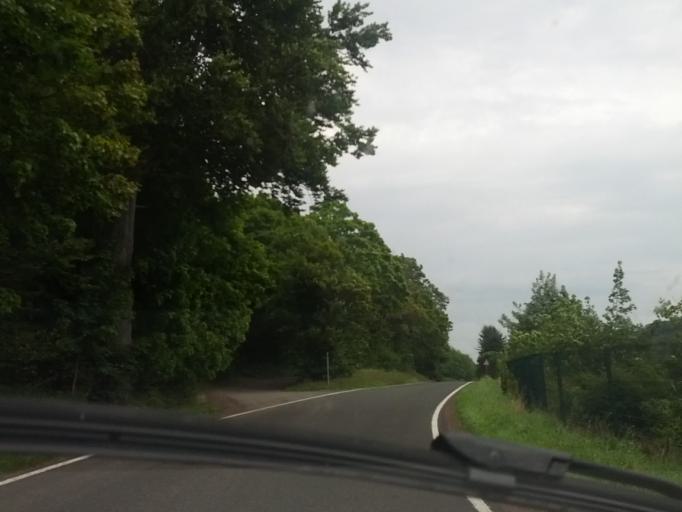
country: DE
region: Thuringia
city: Friedrichroda
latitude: 50.8644
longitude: 10.5833
